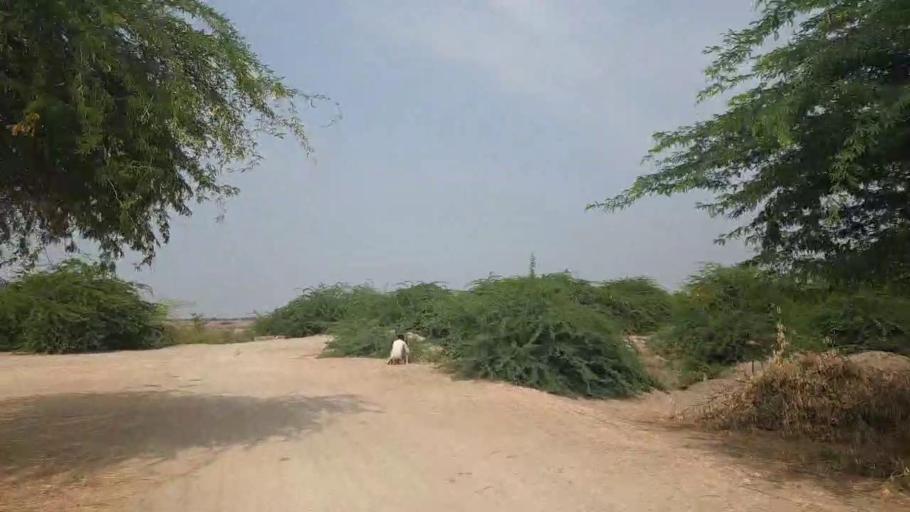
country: PK
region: Sindh
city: Badin
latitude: 24.5648
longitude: 68.7340
